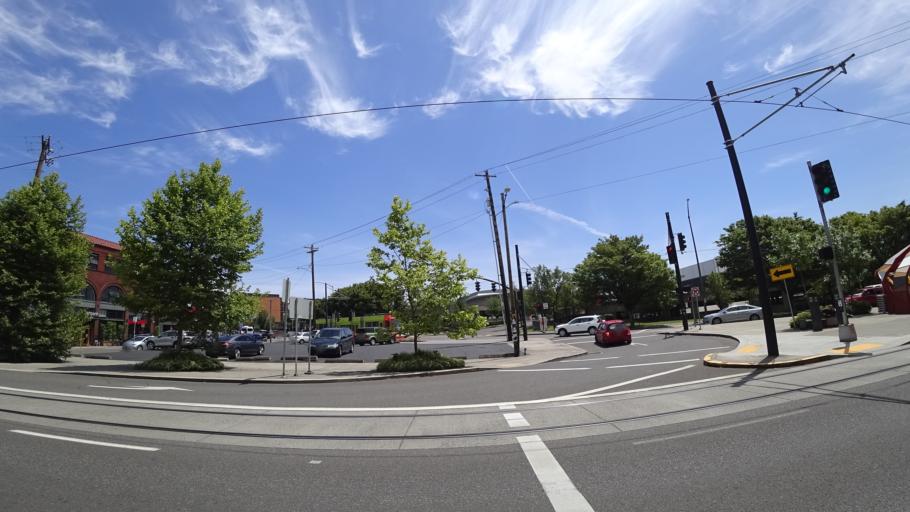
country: US
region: Oregon
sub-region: Multnomah County
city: Portland
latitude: 45.5347
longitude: -122.6692
